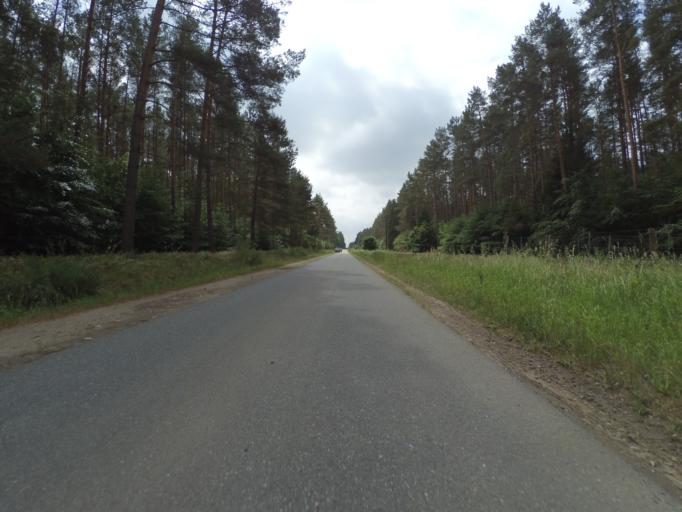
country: DE
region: Mecklenburg-Vorpommern
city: Malchow
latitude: 53.5538
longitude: 12.4157
